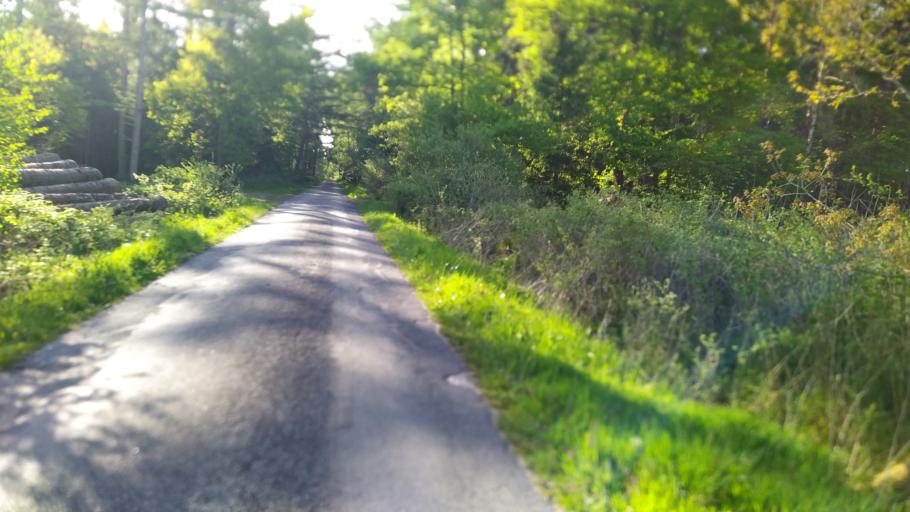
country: DE
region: Lower Saxony
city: Farven
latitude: 53.4044
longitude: 9.3475
